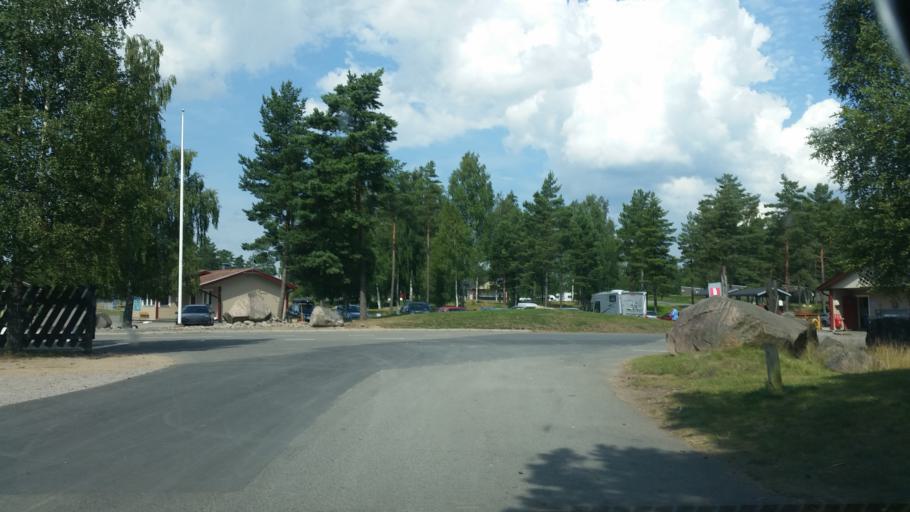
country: SE
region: Vaestra Goetaland
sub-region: Skara Kommun
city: Axvall
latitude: 58.4110
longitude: 13.5555
